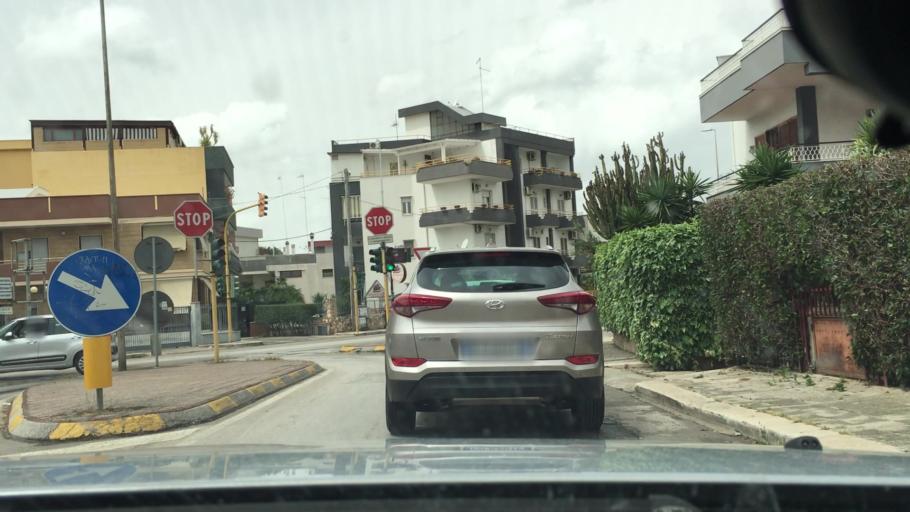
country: IT
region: Apulia
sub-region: Provincia di Bari
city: Capurso
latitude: 41.0508
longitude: 16.9178
